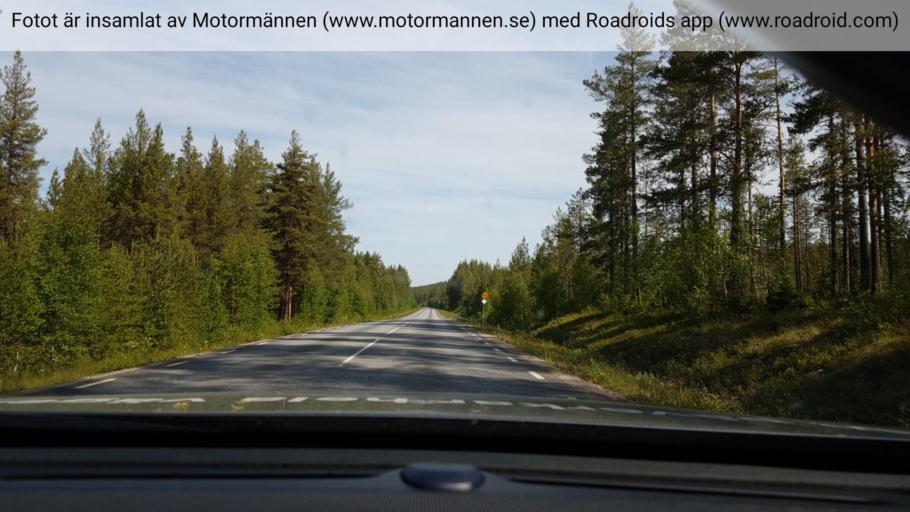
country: SE
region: Vaesterbotten
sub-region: Dorotea Kommun
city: Dorotea
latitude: 64.2824
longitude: 16.3438
